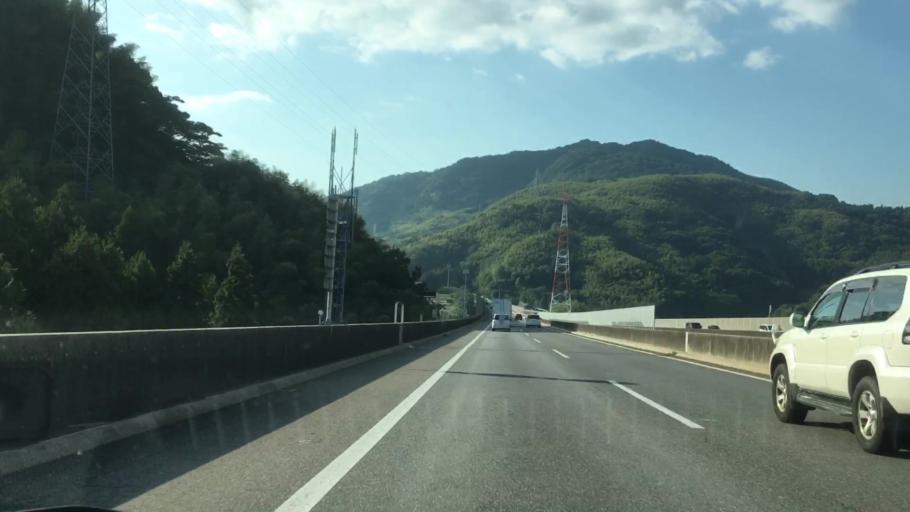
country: JP
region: Yamaguchi
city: Tokuyama
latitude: 34.0848
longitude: 131.7839
